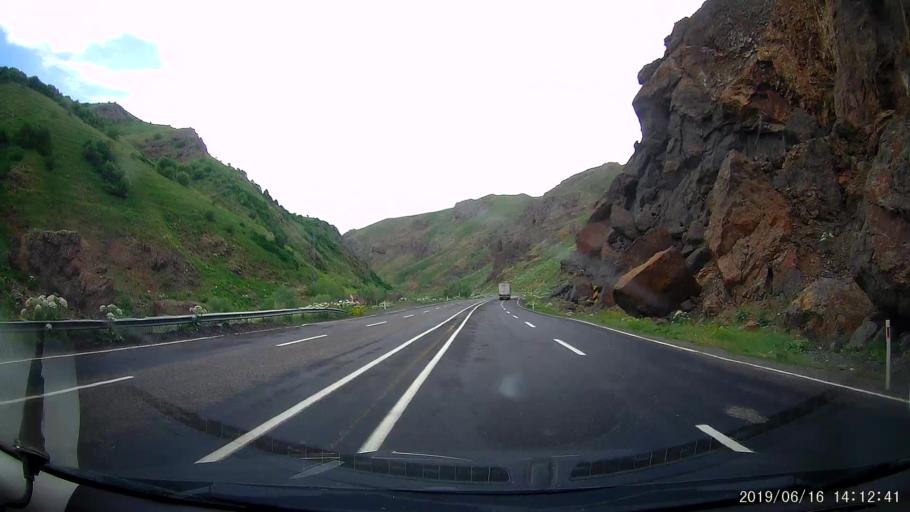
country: TR
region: Agri
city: Tahir
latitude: 39.7986
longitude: 42.5323
